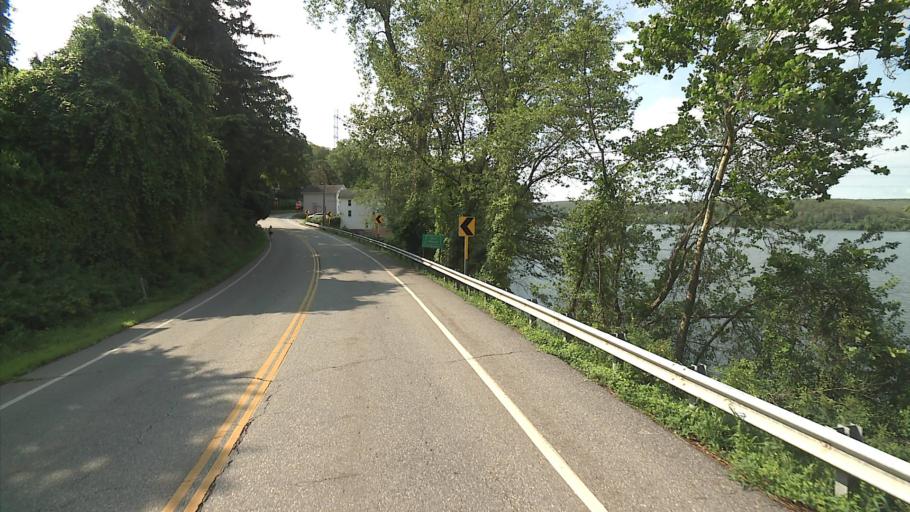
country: US
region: Connecticut
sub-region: Middlesex County
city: East Haddam
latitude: 41.4641
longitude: -72.4649
